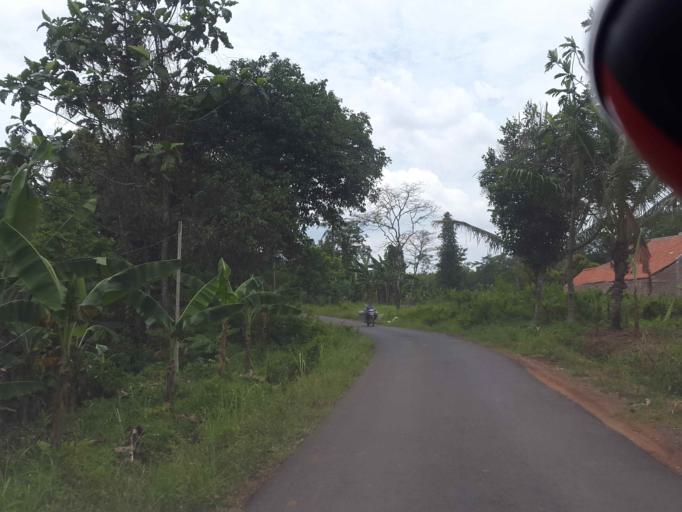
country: ID
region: Lampung
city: Natar
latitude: -5.3183
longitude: 105.2485
